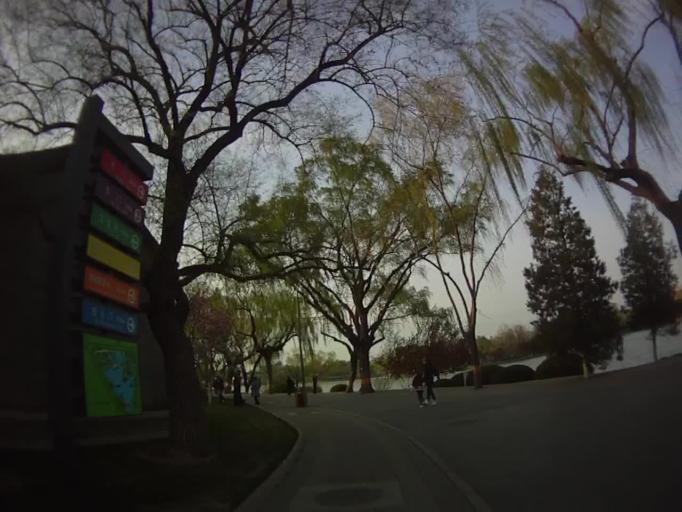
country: CN
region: Beijing
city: Longtan
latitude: 39.8746
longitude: 116.4353
